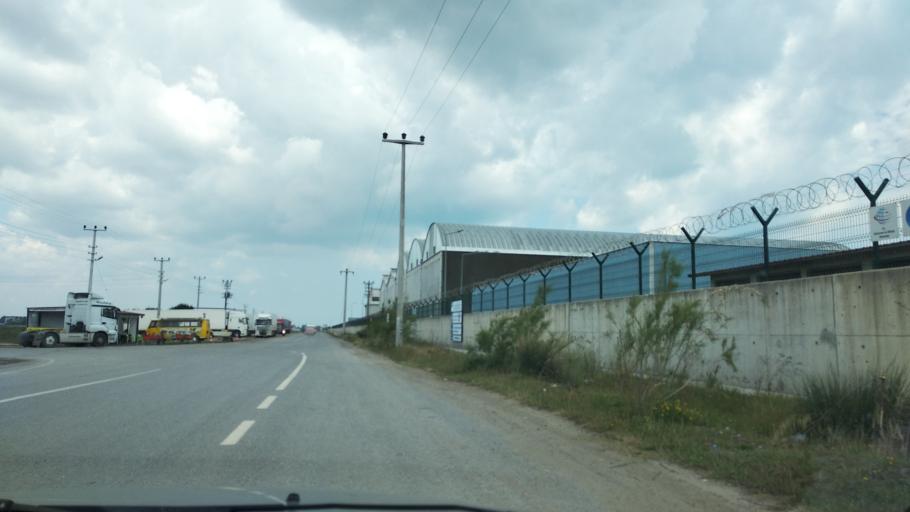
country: TR
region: Sakarya
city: Karasu
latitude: 41.1169
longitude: 30.6747
